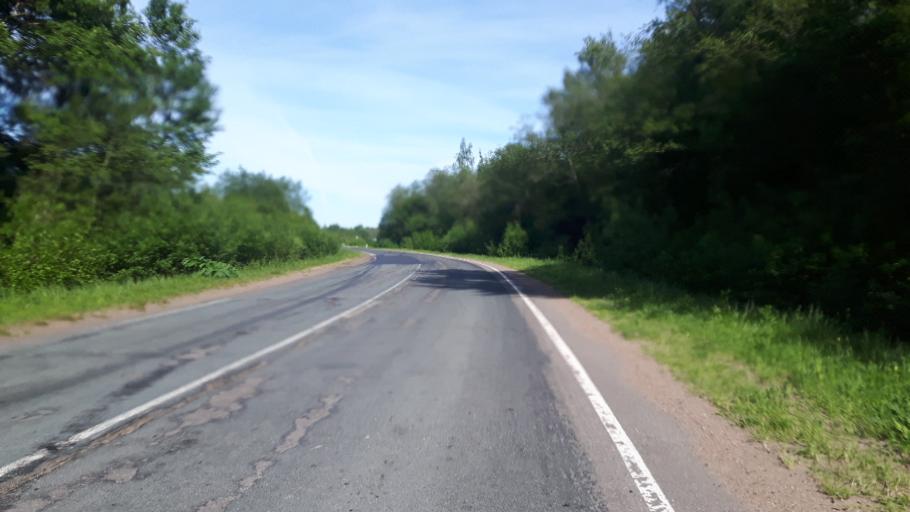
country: RU
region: Leningrad
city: Ivangorod
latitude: 59.4162
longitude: 28.3712
